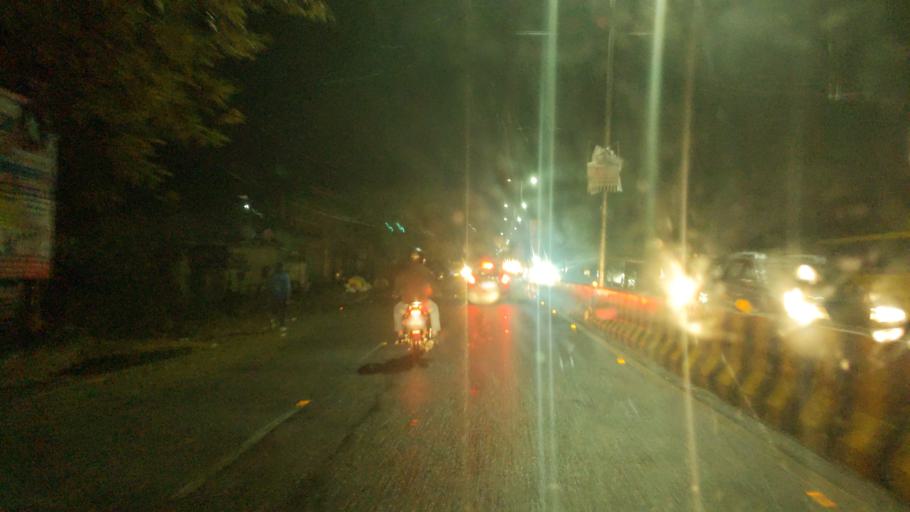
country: IN
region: Uttarakhand
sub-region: Naini Tal
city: Haldwani
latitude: 29.2564
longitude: 79.5427
